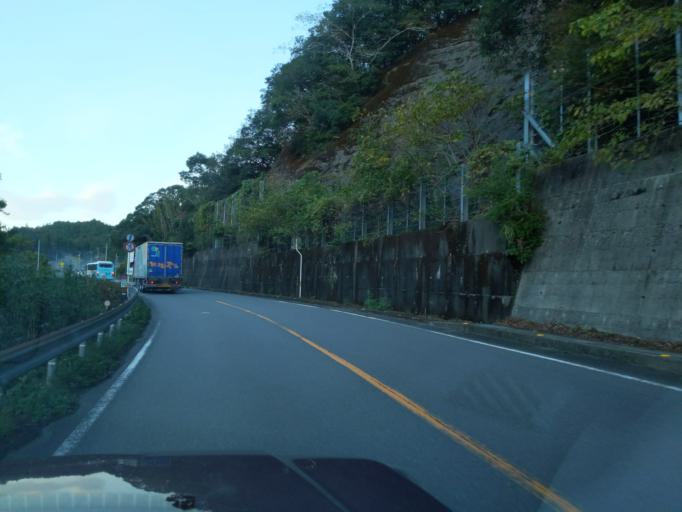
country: JP
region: Tokushima
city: Anan
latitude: 33.7126
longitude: 134.4774
